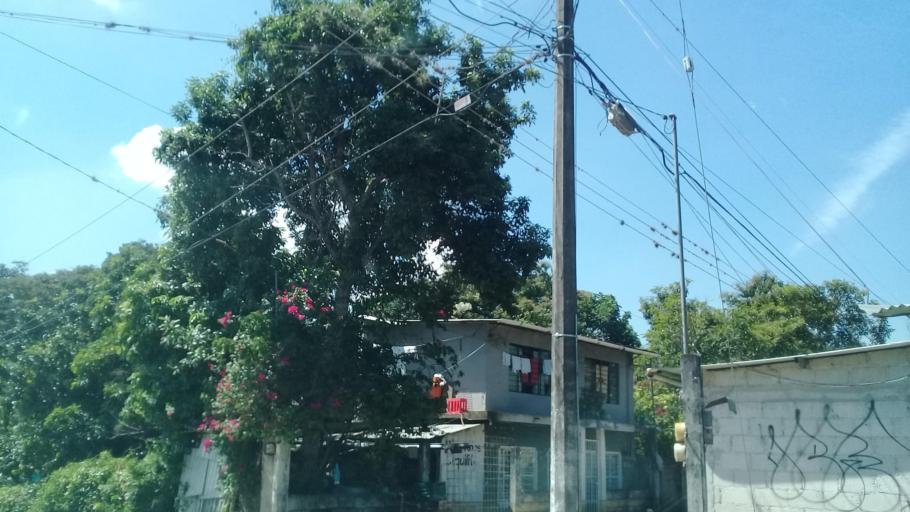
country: MX
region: Veracruz
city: Amatlan de los Reyes
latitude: 18.8415
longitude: -96.9169
